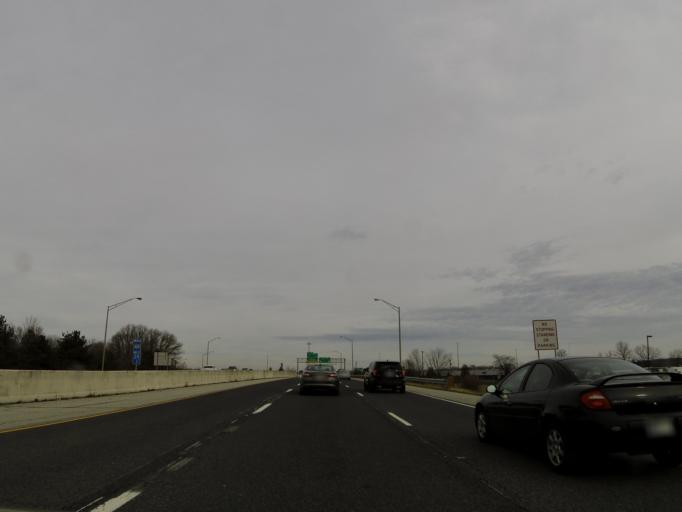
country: US
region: Indiana
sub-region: Boone County
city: Zionsville
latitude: 39.9231
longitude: -86.2683
